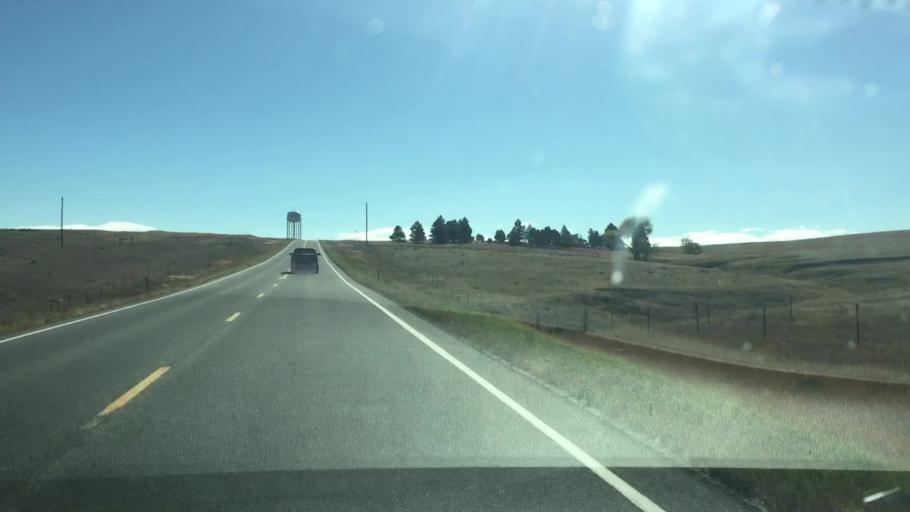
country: US
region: Colorado
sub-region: Elbert County
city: Kiowa
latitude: 39.3433
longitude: -104.4479
